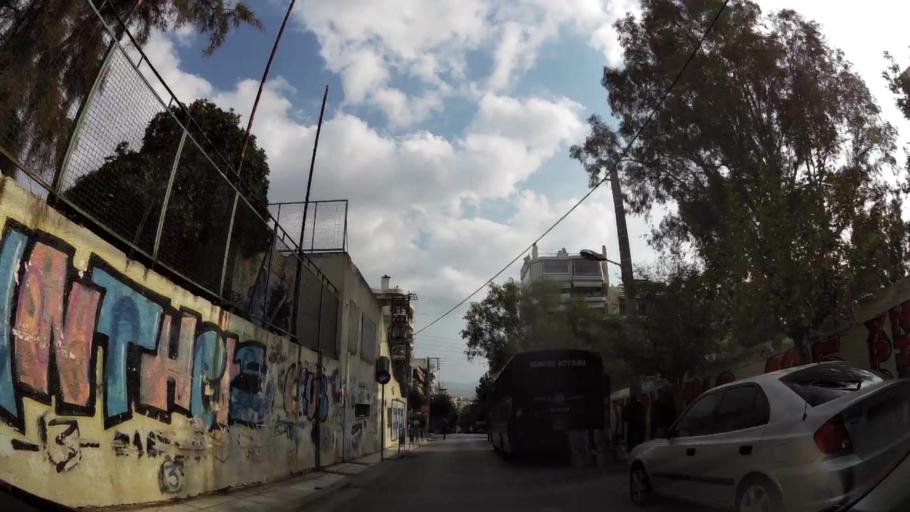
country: GR
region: Attica
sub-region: Nomarchia Athinas
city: Nea Smyrni
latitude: 37.9457
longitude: 23.7212
